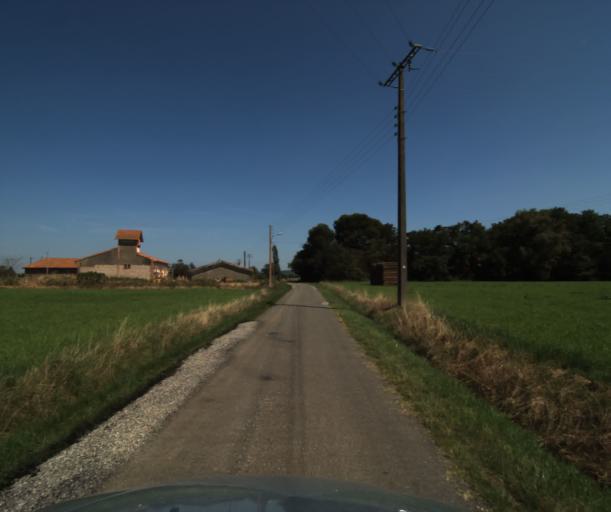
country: FR
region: Midi-Pyrenees
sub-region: Departement de la Haute-Garonne
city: Labastidette
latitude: 43.4396
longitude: 1.2651
